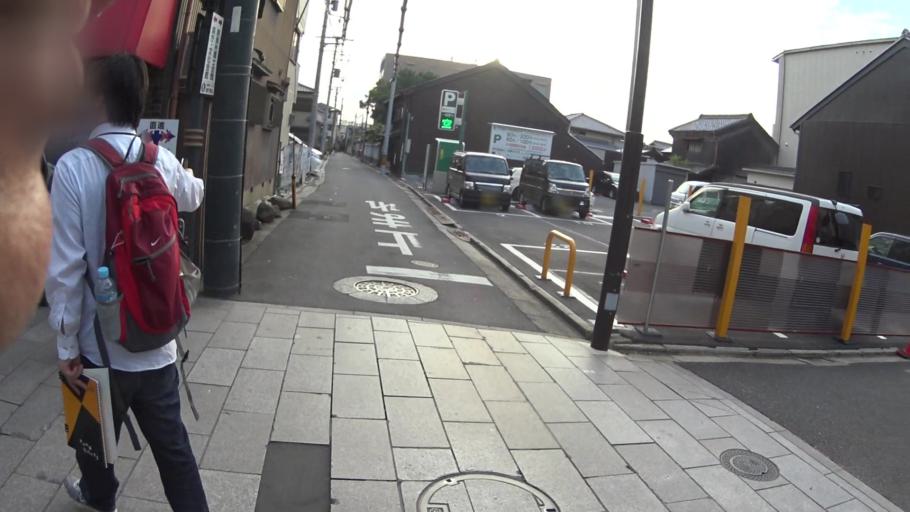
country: JP
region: Nara
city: Nara-shi
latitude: 34.6857
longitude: 135.8289
